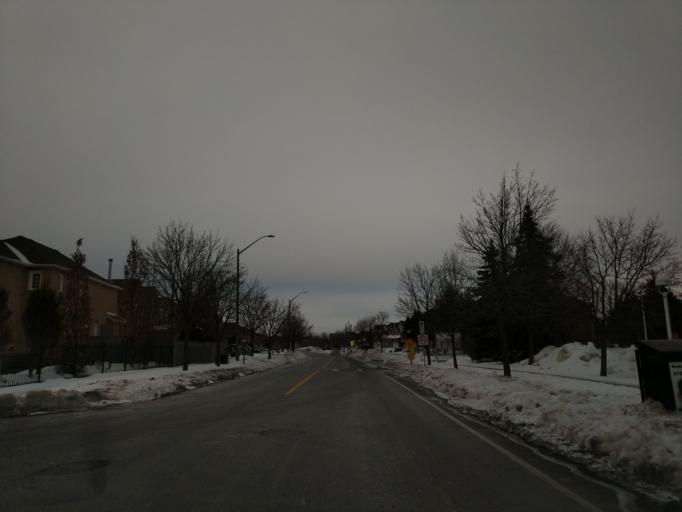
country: CA
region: Ontario
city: Markham
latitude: 43.8453
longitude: -79.2744
